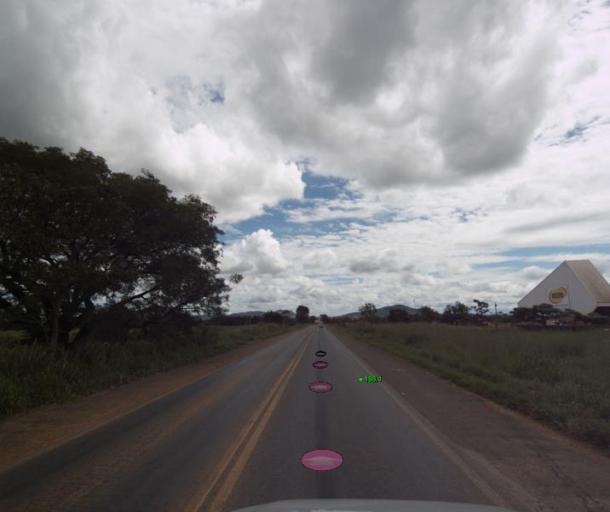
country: BR
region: Goias
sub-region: Uruacu
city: Uruacu
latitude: -14.4674
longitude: -49.1561
